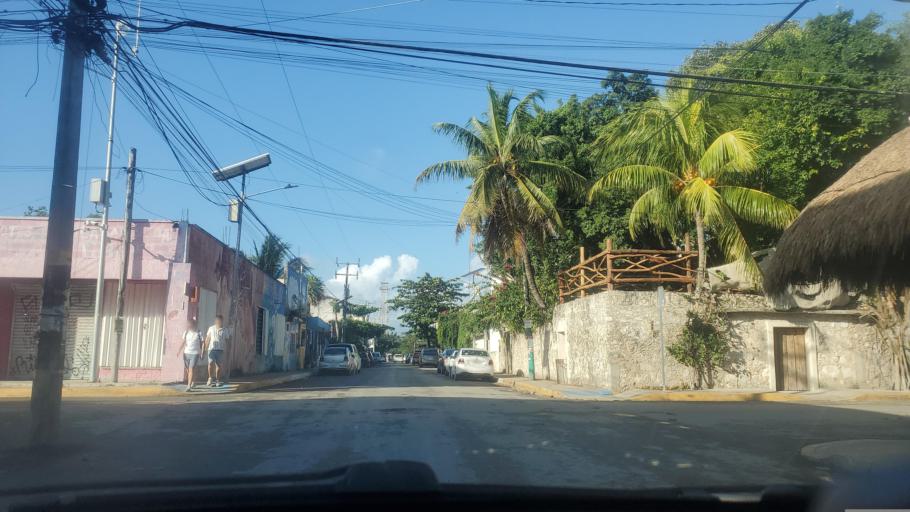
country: MX
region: Quintana Roo
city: Tulum
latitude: 20.2109
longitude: -87.4588
